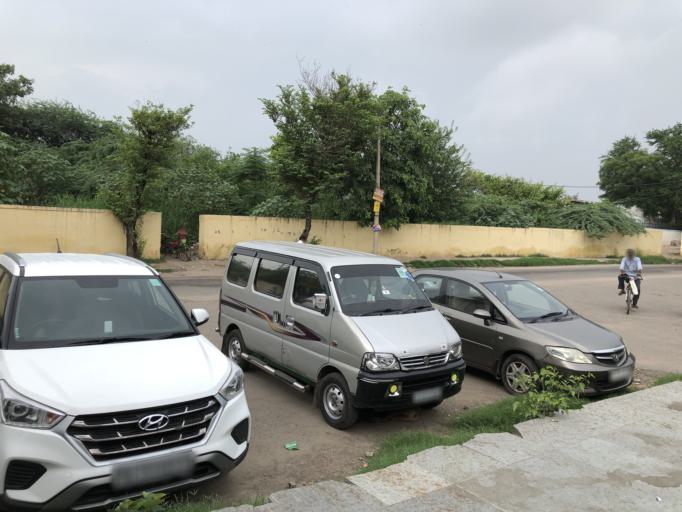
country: IN
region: NCT
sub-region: New Delhi
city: New Delhi
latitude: 28.5760
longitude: 77.2503
